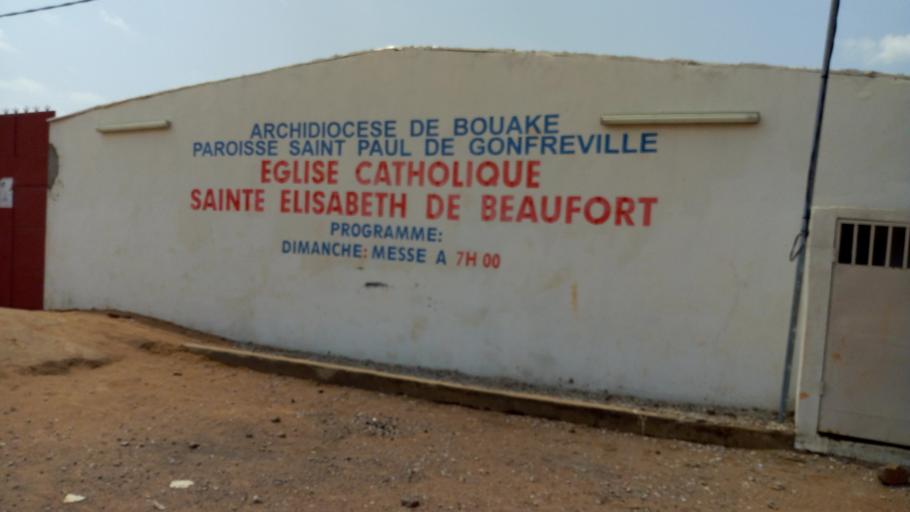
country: CI
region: Vallee du Bandama
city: Bouake
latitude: 7.7177
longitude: -5.0440
